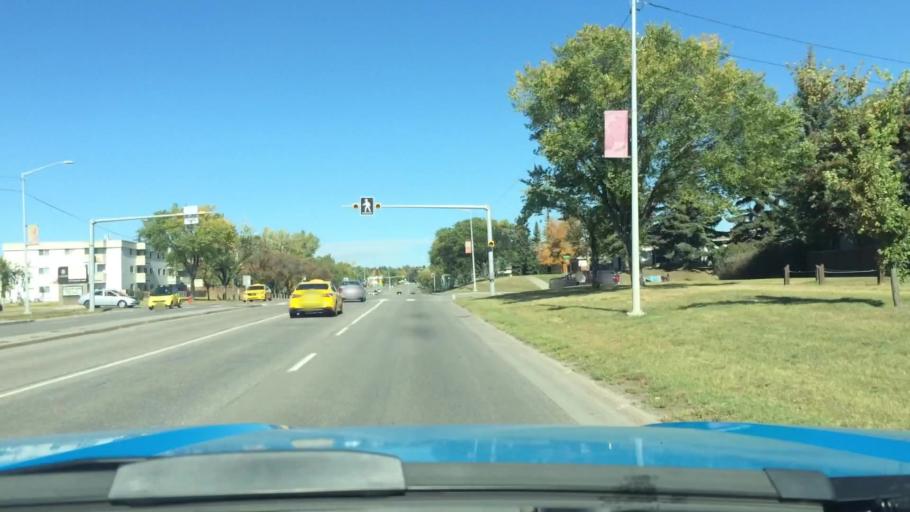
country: CA
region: Alberta
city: Calgary
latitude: 51.1130
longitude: -114.0639
